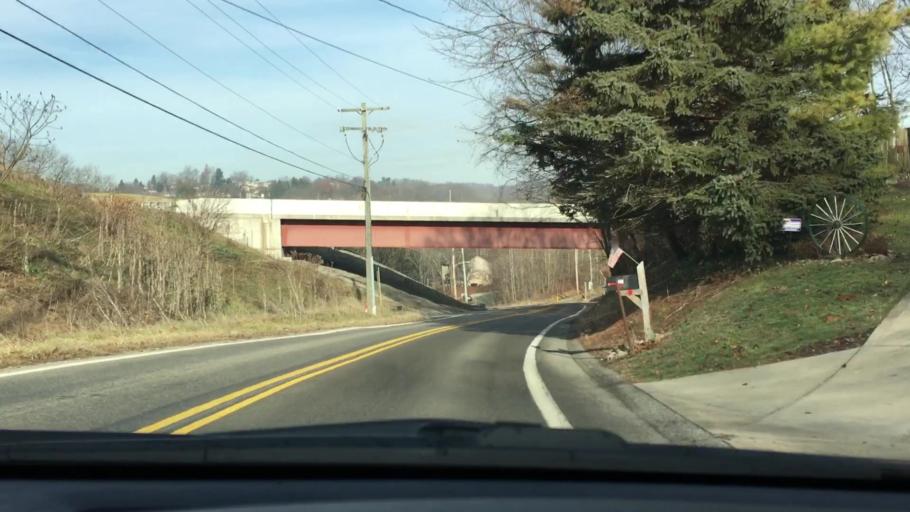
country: US
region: Pennsylvania
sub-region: Allegheny County
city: Jefferson Hills
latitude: 40.2768
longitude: -79.9495
